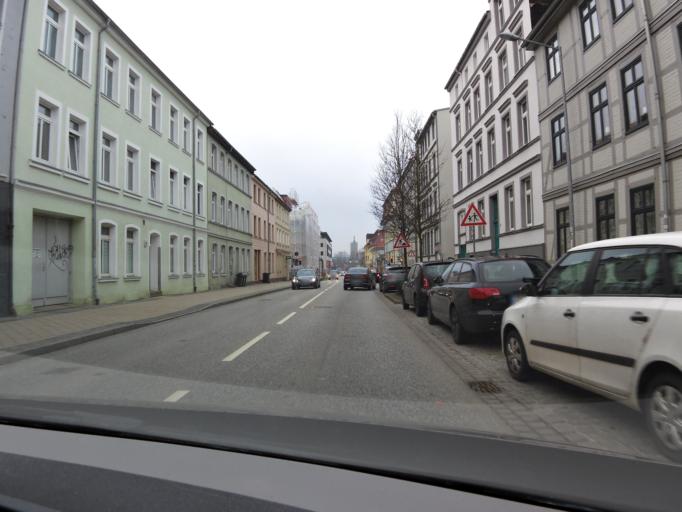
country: DE
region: Mecklenburg-Vorpommern
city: Schelfstadt
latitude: 53.6327
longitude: 11.4219
